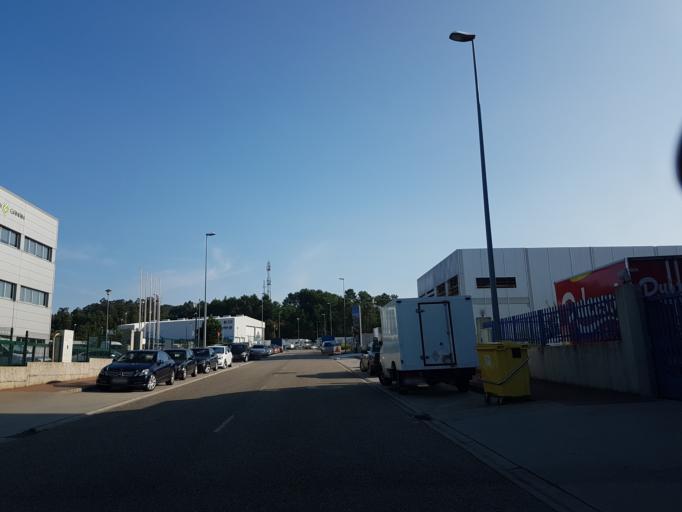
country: ES
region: Galicia
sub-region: Provincia de Pontevedra
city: Porrino
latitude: 42.1878
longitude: -8.6209
